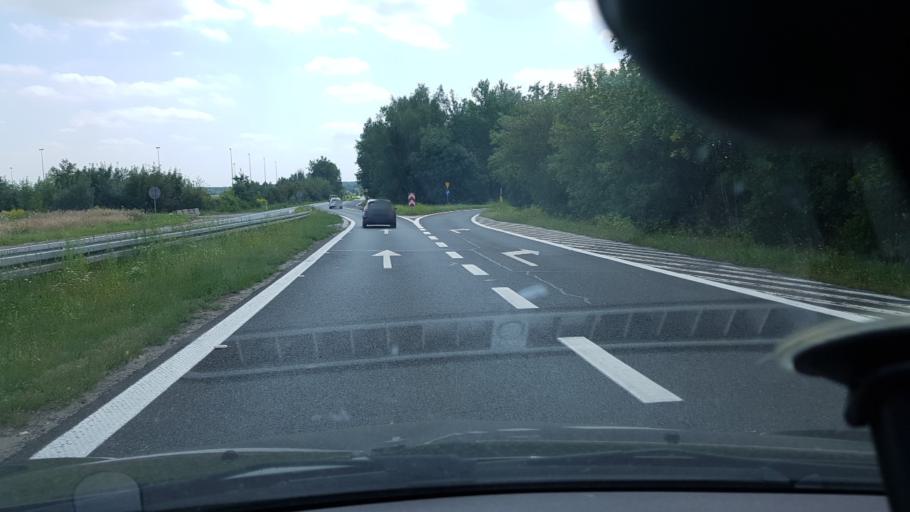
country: PL
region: Silesian Voivodeship
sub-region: Powiat bierunsko-ledzinski
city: Bierun
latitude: 50.0991
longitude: 19.0985
